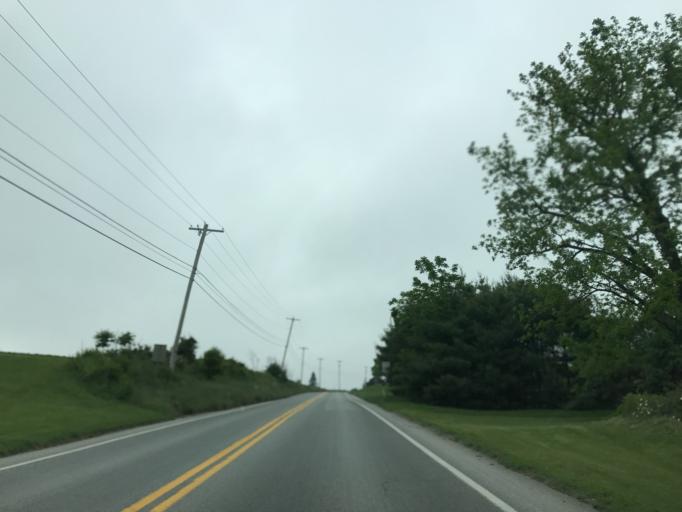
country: US
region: Pennsylvania
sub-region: York County
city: Susquehanna Trails
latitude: 39.8347
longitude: -76.4107
